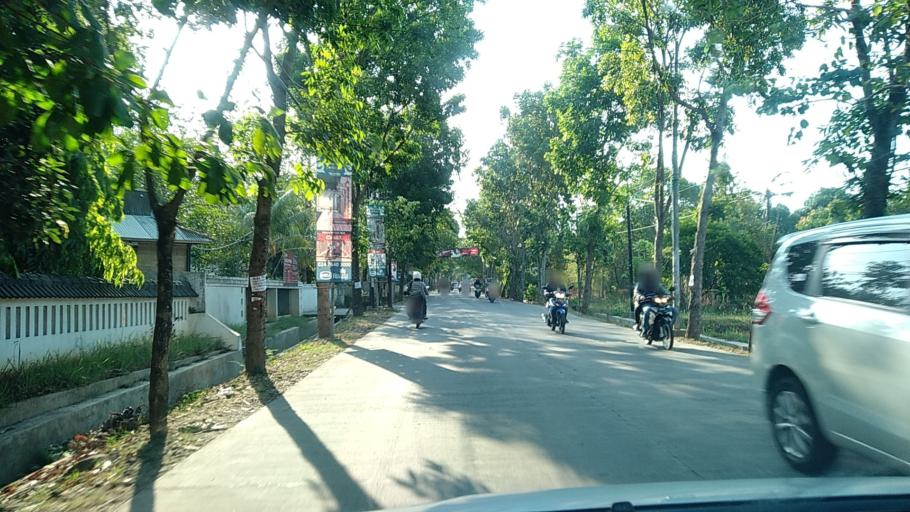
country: ID
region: Central Java
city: Semarang
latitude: -7.0643
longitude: 110.4257
